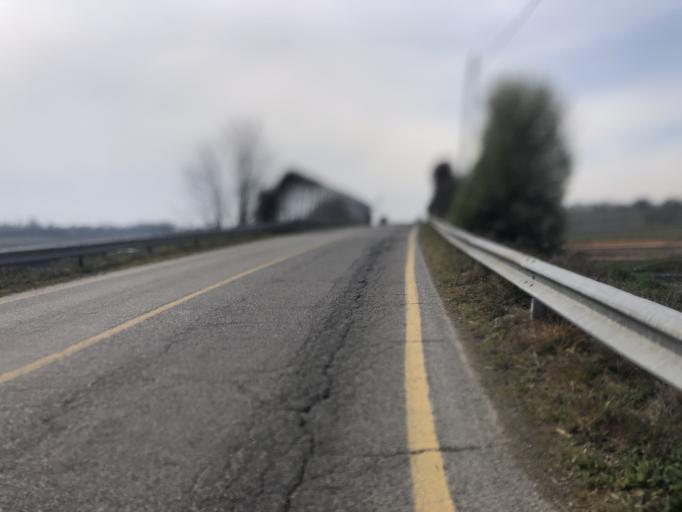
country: IT
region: Veneto
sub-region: Provincia di Verona
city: San Giorgio in Salici
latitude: 45.4222
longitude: 10.7815
